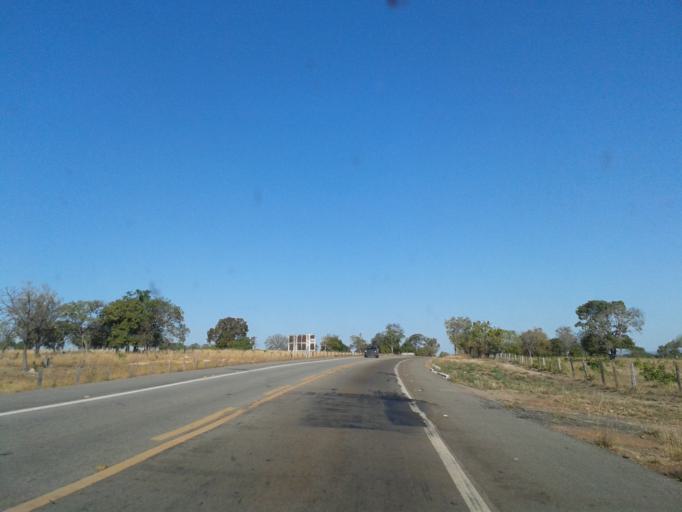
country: BR
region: Goias
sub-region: Mozarlandia
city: Mozarlandia
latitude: -15.2569
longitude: -50.4951
